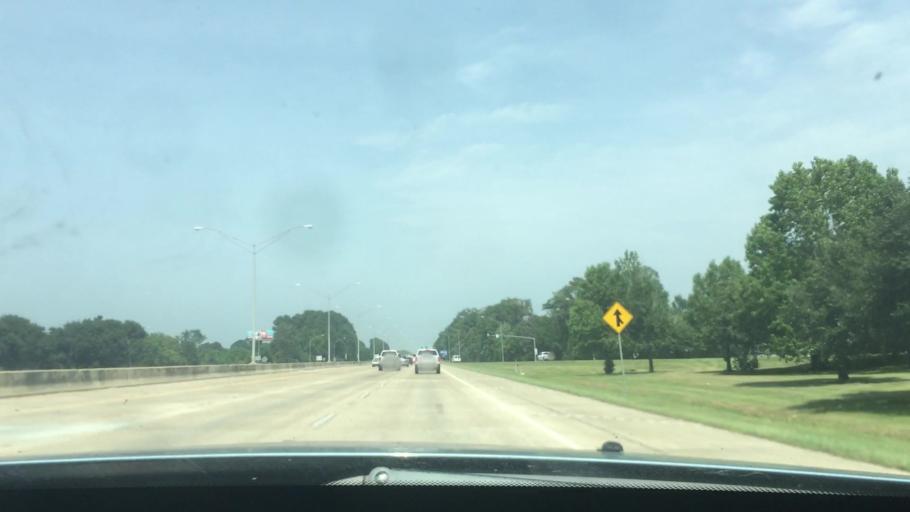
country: US
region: Louisiana
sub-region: East Baton Rouge Parish
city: Shenandoah
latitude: 30.4383
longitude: -91.0235
